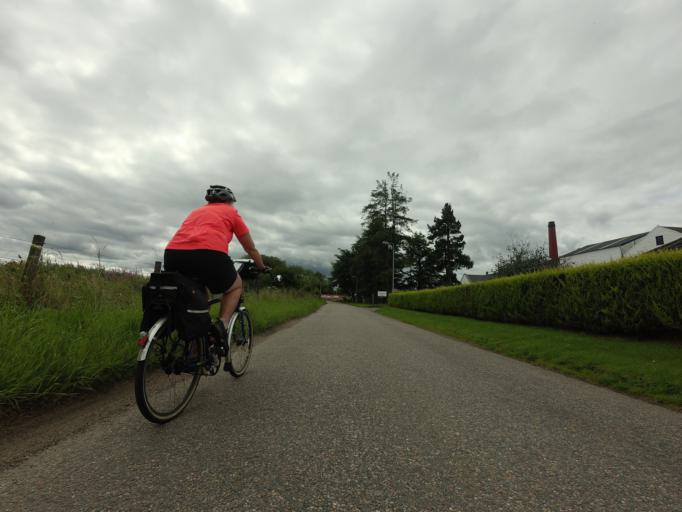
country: GB
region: Scotland
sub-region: Moray
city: Forres
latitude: 57.6141
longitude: -3.6191
